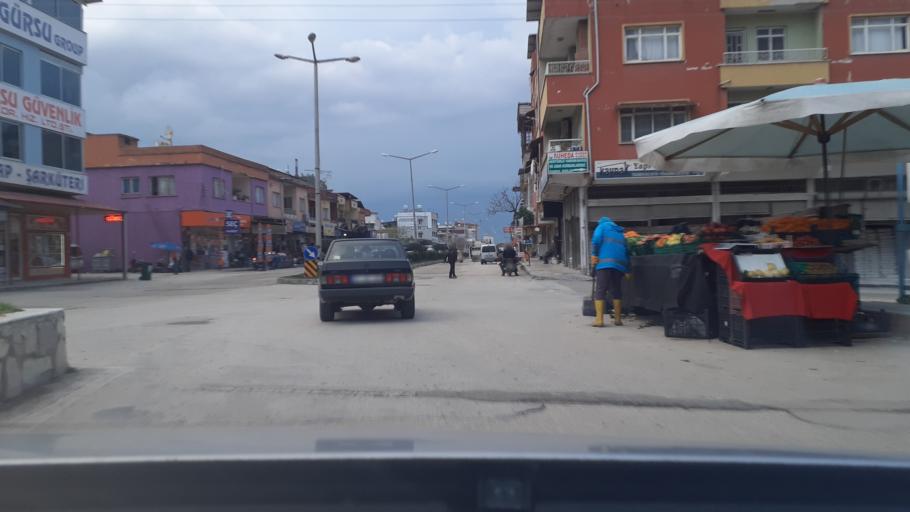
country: TR
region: Hatay
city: Kirikhan
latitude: 36.4950
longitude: 36.3596
